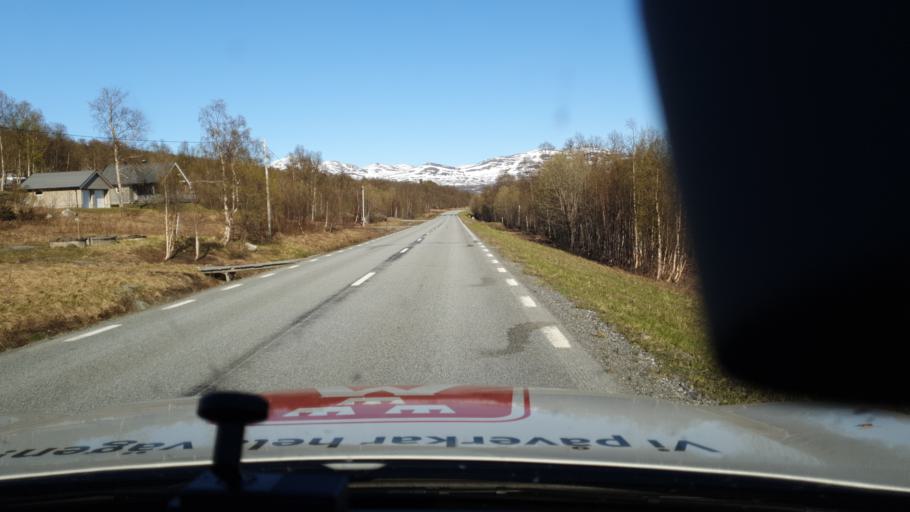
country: NO
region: Nordland
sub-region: Rana
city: Mo i Rana
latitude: 66.0407
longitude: 15.0089
